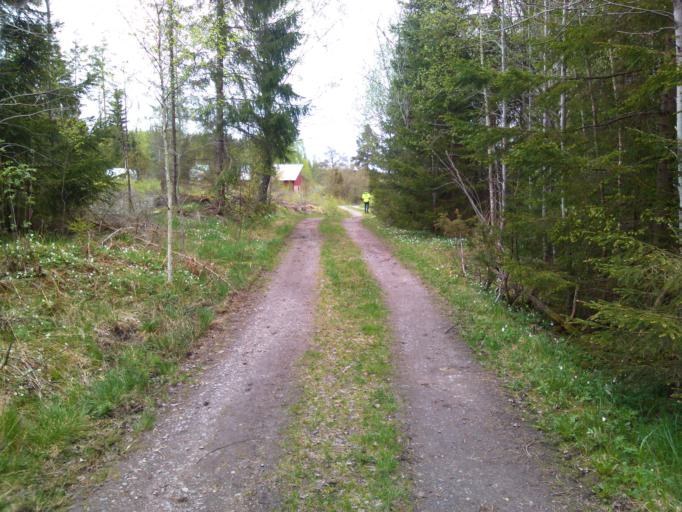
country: SE
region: Stockholm
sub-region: Norrtalje Kommun
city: Norrtalje
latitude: 59.6559
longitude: 18.6621
